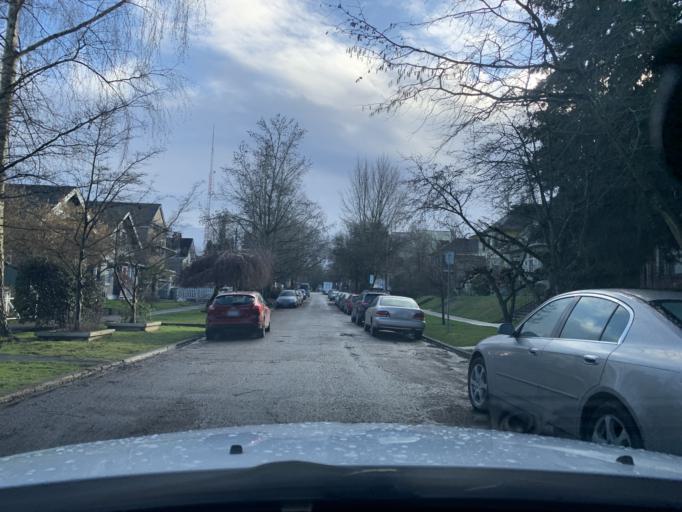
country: US
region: Washington
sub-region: King County
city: Seattle
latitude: 47.6216
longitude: -122.3101
